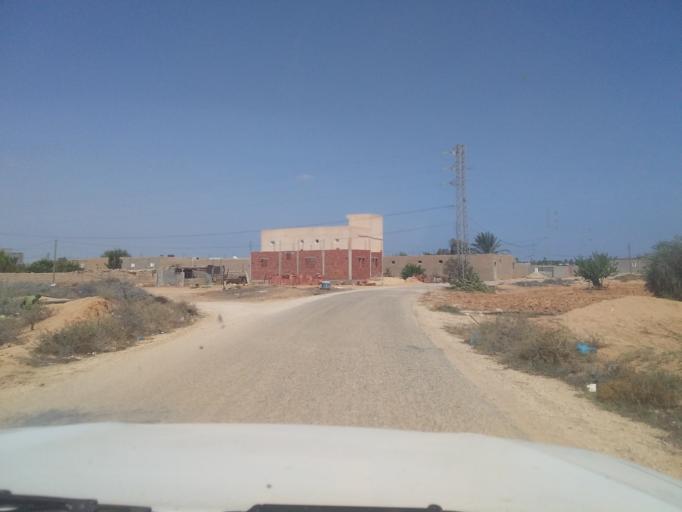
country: TN
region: Qabis
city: Matmata
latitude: 33.5932
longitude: 10.2859
